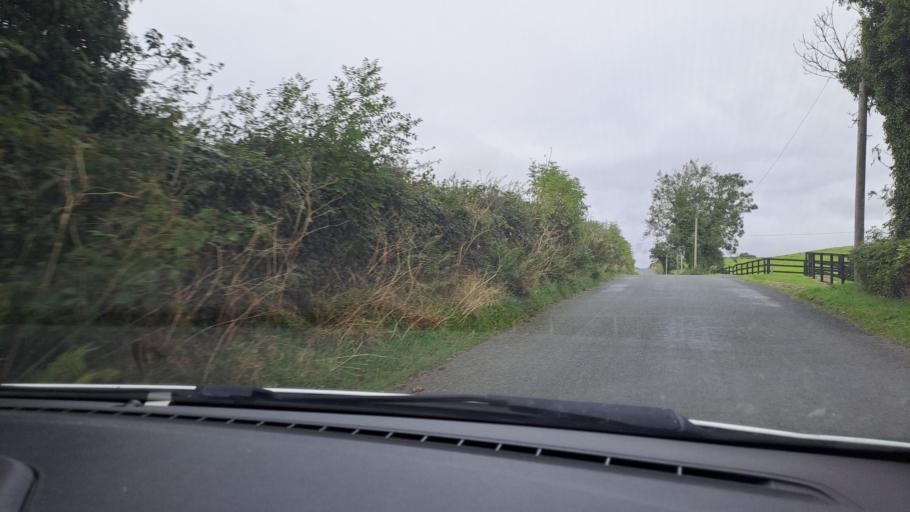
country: IE
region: Ulster
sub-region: County Monaghan
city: Carrickmacross
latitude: 54.0025
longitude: -6.8037
